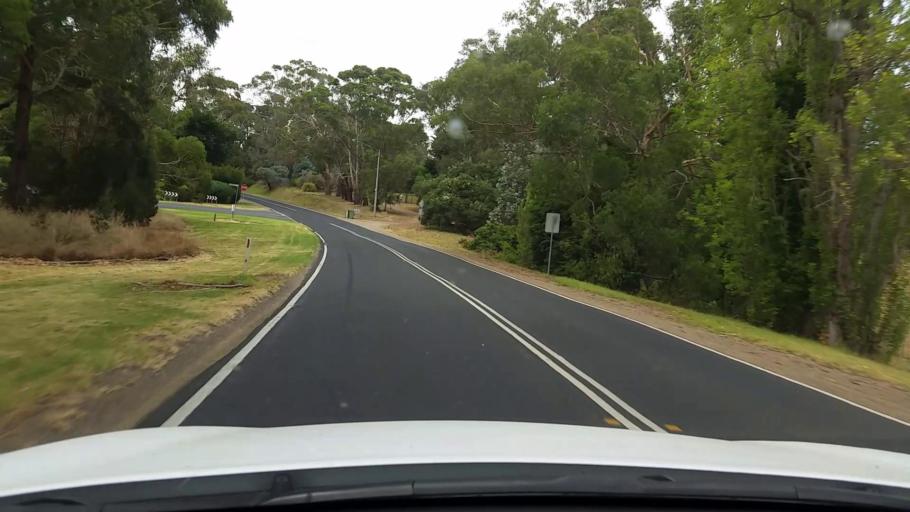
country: AU
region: Victoria
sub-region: Mornington Peninsula
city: Merricks
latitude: -38.4292
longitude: 145.0416
